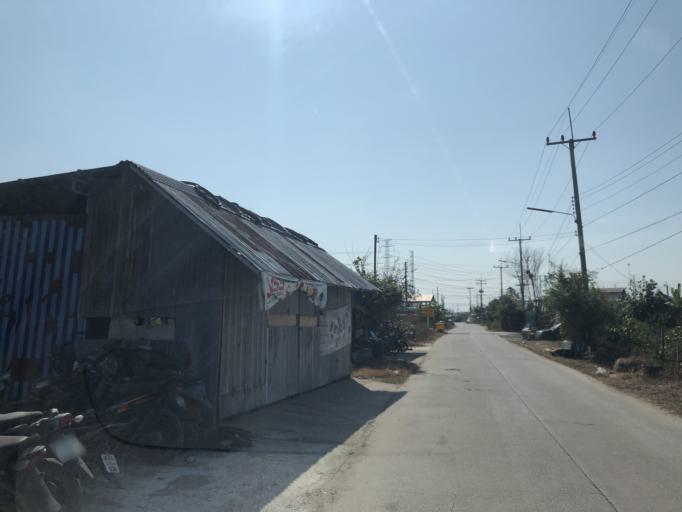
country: TH
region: Chachoengsao
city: Bang Pakong
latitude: 13.5174
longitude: 101.0221
